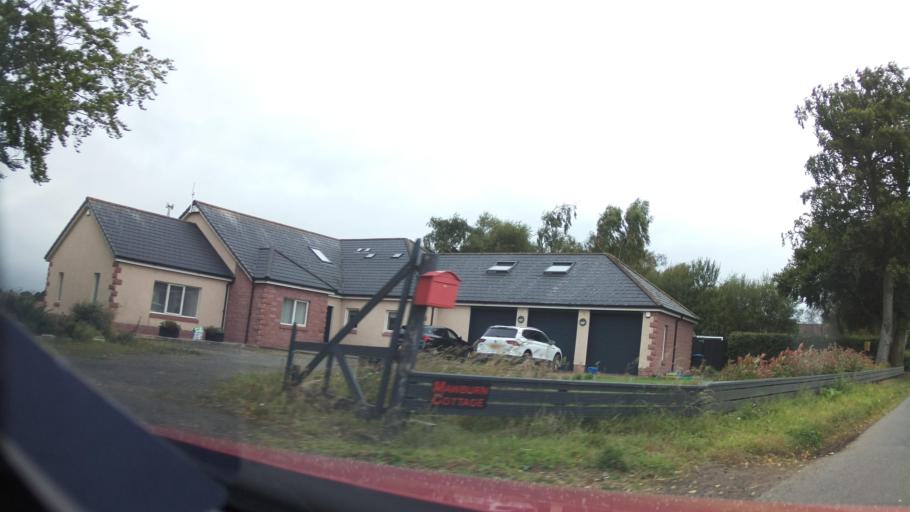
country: GB
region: Scotland
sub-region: Perth and Kinross
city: Milnathort
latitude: 56.2419
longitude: -3.3722
